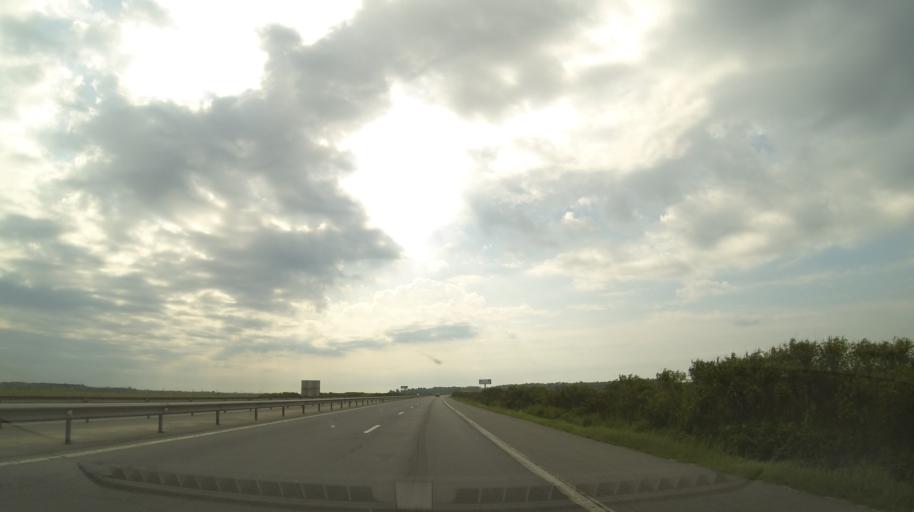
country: RO
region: Dambovita
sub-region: Comuna Uliesti
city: Uliesti
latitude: 44.6202
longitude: 25.4382
